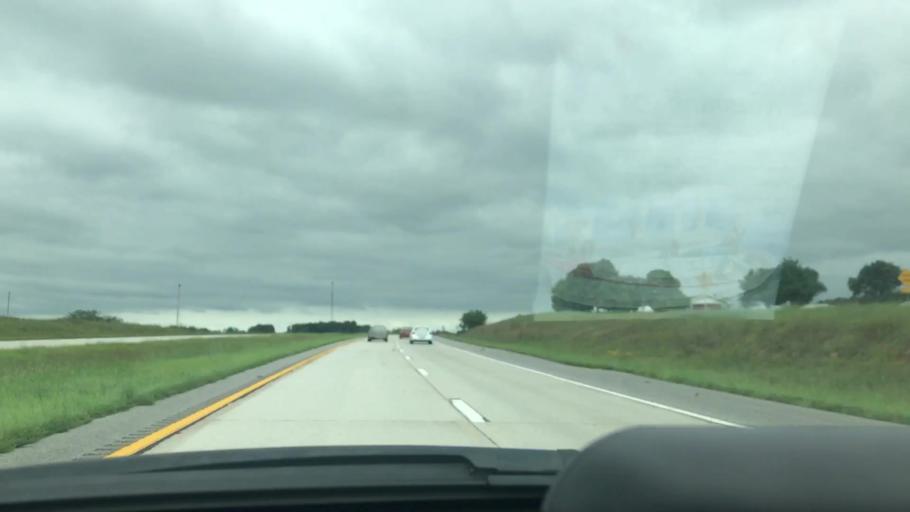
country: US
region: Missouri
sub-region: Greene County
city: Fair Grove
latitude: 37.4440
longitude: -93.1441
